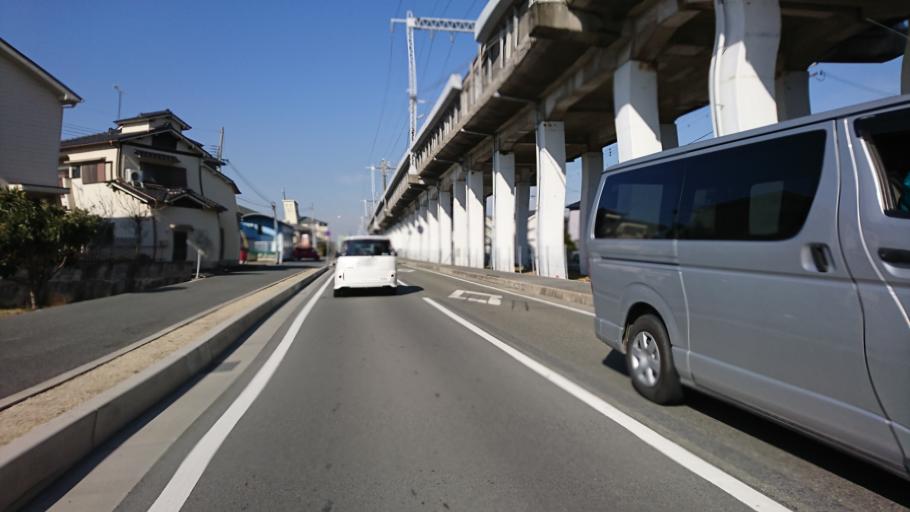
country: JP
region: Hyogo
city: Kakogawacho-honmachi
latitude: 34.7684
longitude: 134.7969
